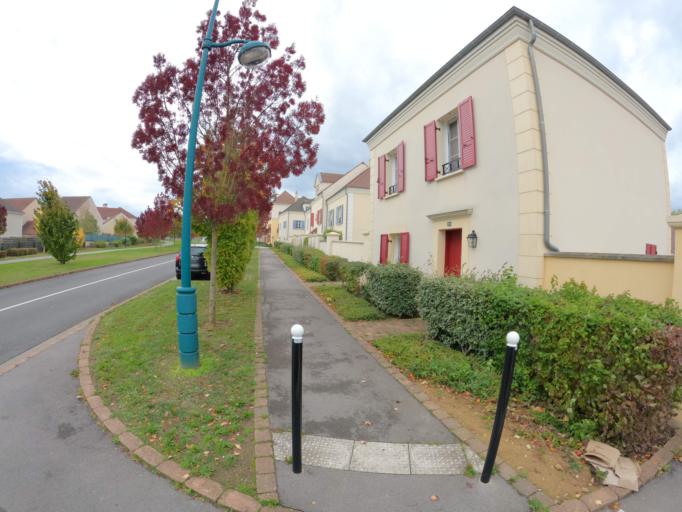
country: FR
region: Ile-de-France
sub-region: Departement de Seine-et-Marne
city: Magny-le-Hongre
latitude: 48.8720
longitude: 2.8167
